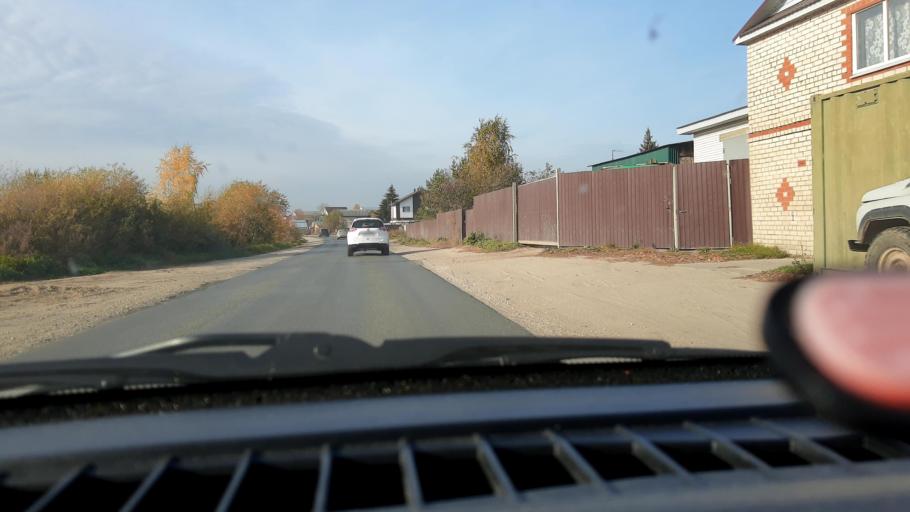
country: RU
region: Nizjnij Novgorod
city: Neklyudovo
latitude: 56.4167
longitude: 43.9702
